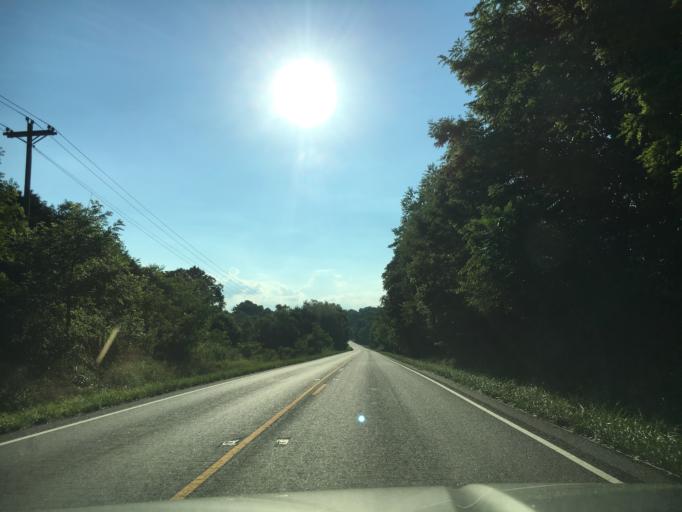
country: US
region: Virginia
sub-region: City of Bedford
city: Bedford
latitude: 37.2380
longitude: -79.5831
